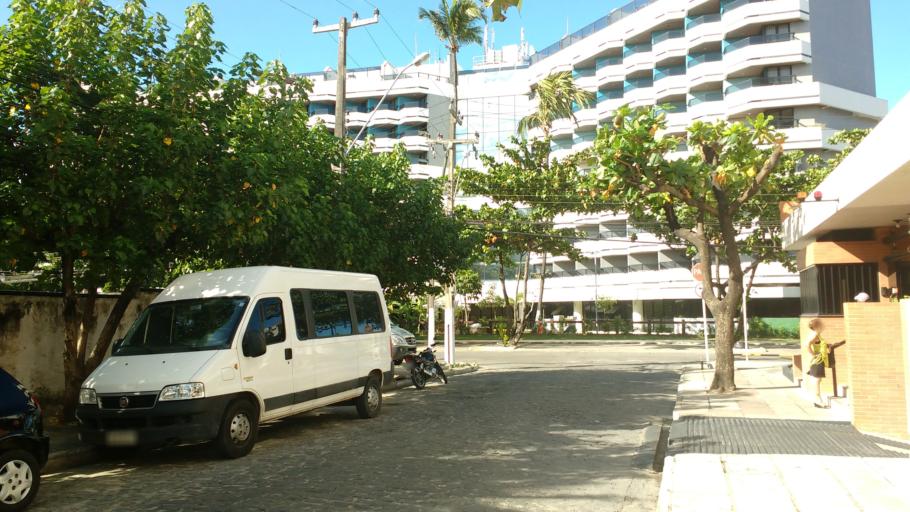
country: BR
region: Alagoas
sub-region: Maceio
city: Maceio
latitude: -9.6490
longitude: -35.7012
